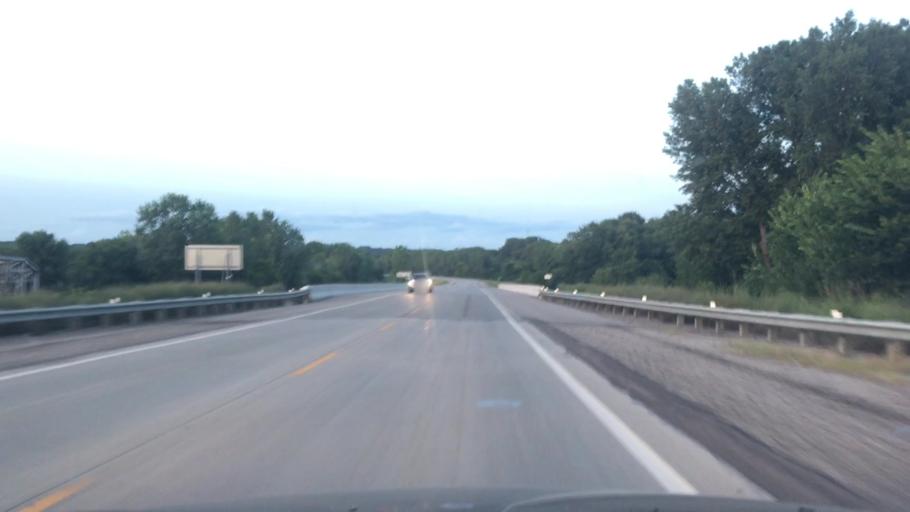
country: US
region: Minnesota
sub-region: Redwood County
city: Redwood Falls
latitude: 44.5409
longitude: -95.0037
